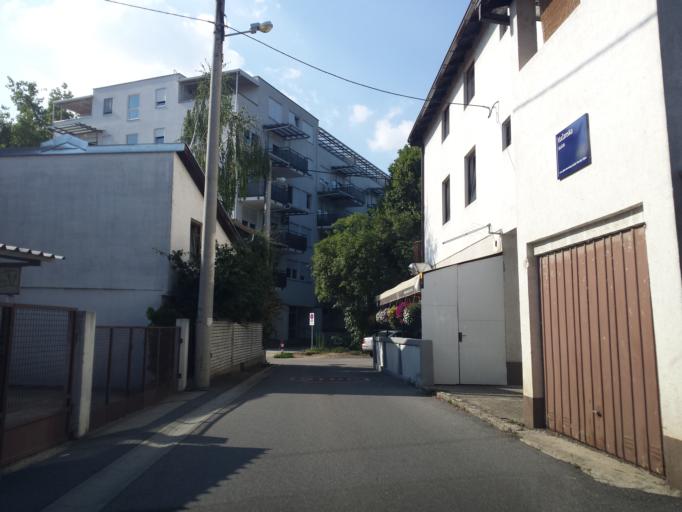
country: HR
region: Grad Zagreb
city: Novi Zagreb
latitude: 45.7985
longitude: 15.9832
